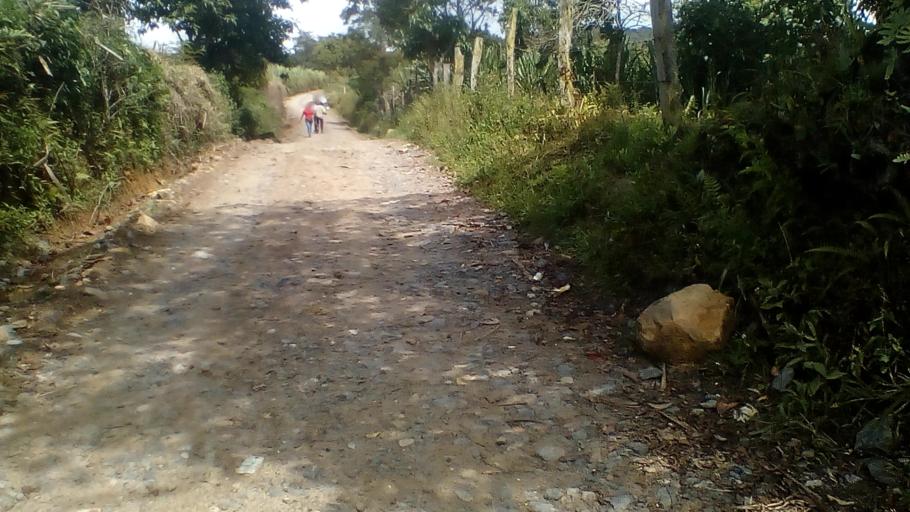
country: CO
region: Boyaca
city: Santana
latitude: 6.0000
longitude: -73.5066
